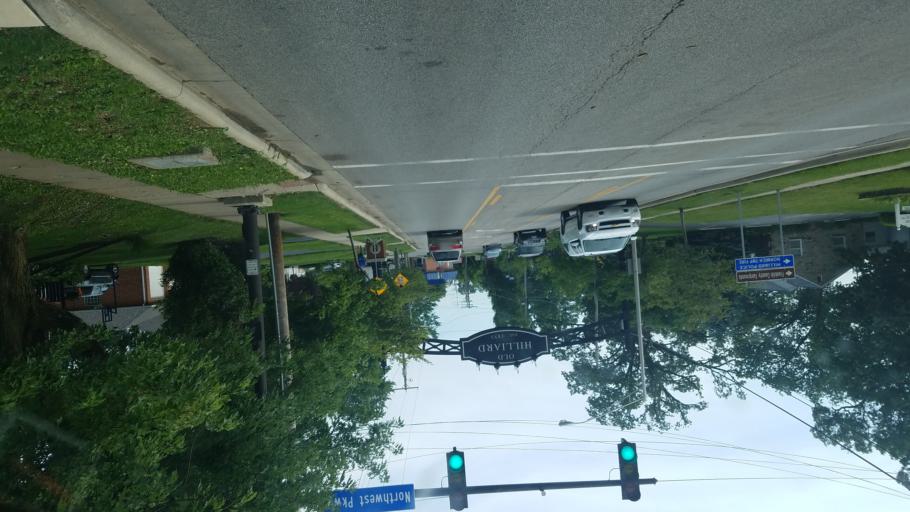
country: US
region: Ohio
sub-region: Franklin County
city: Hilliard
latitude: 40.0377
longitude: -83.1565
